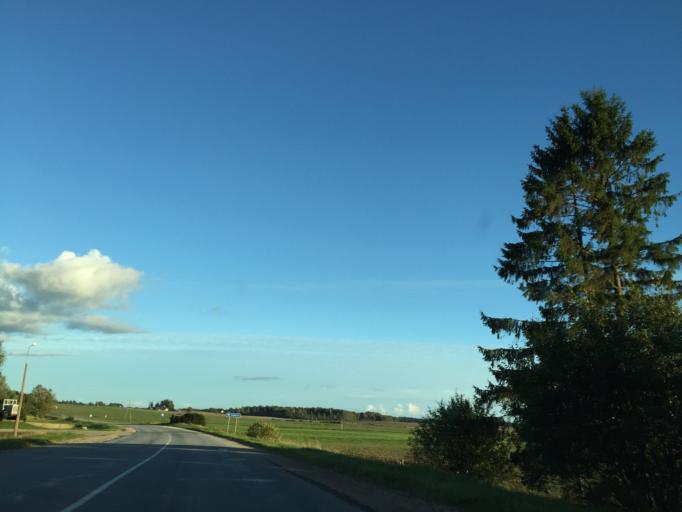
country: LV
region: Saldus Rajons
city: Saldus
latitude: 56.7181
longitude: 22.3899
